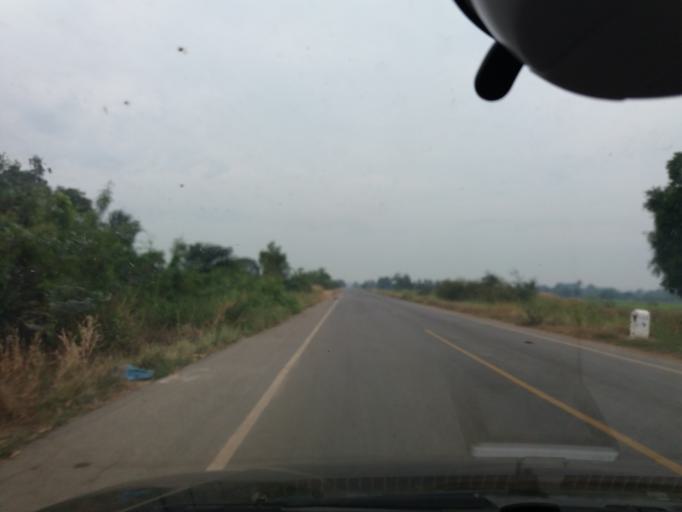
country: TH
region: Suphan Buri
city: Doem Bang Nang Buat
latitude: 14.8977
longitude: 100.1330
